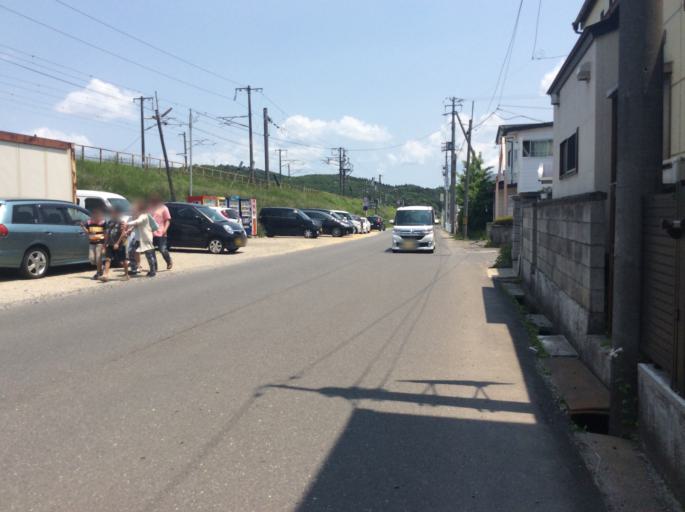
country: JP
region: Fukushima
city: Sukagawa
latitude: 37.1291
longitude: 140.2174
